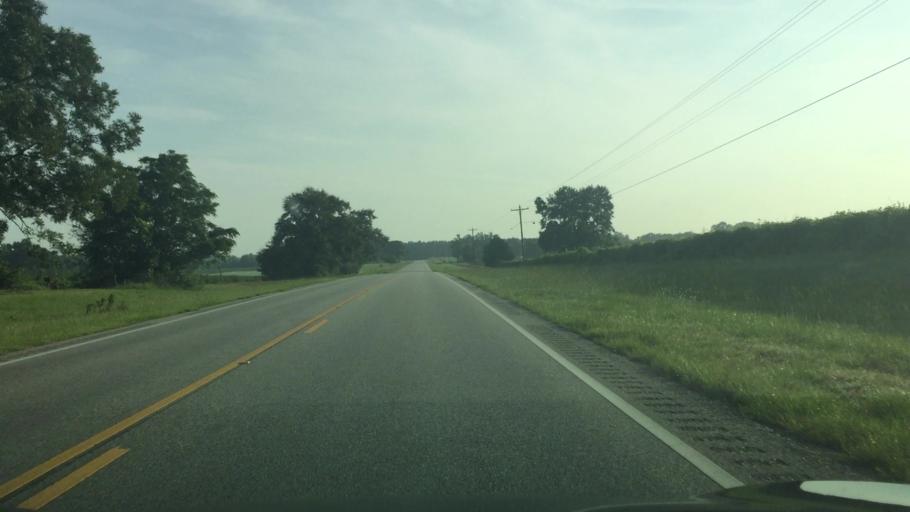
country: US
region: Alabama
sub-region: Covington County
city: Andalusia
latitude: 31.1781
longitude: -86.4567
